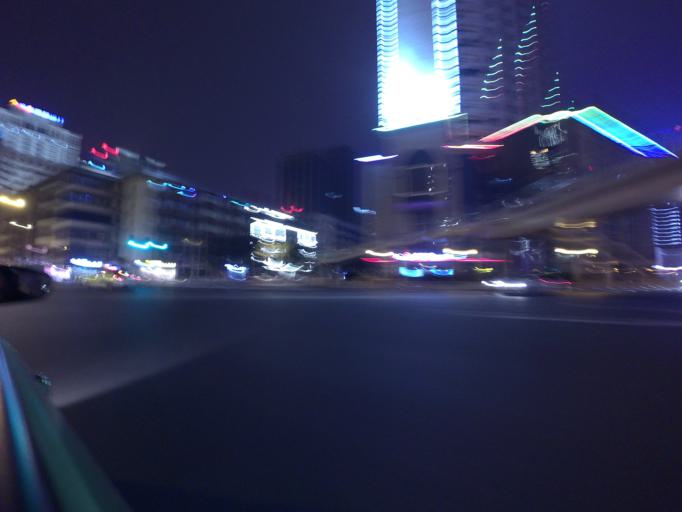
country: CN
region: Sichuan
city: Chengdu
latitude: 30.6571
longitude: 104.0583
